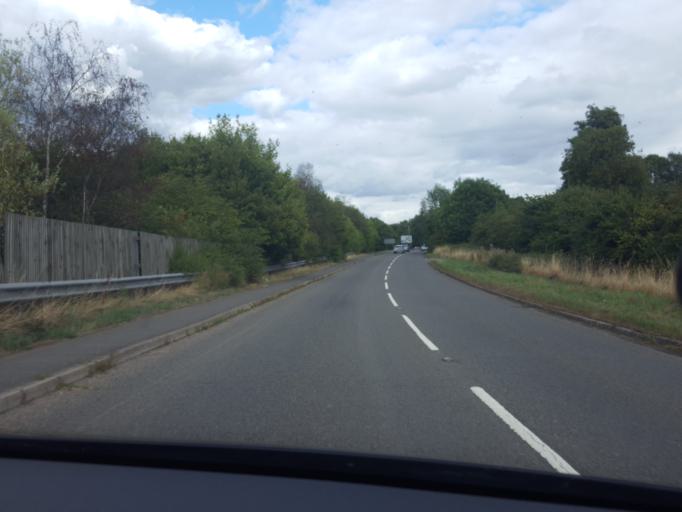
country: GB
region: England
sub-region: Leicestershire
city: Anstey
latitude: 52.6641
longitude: -1.1874
